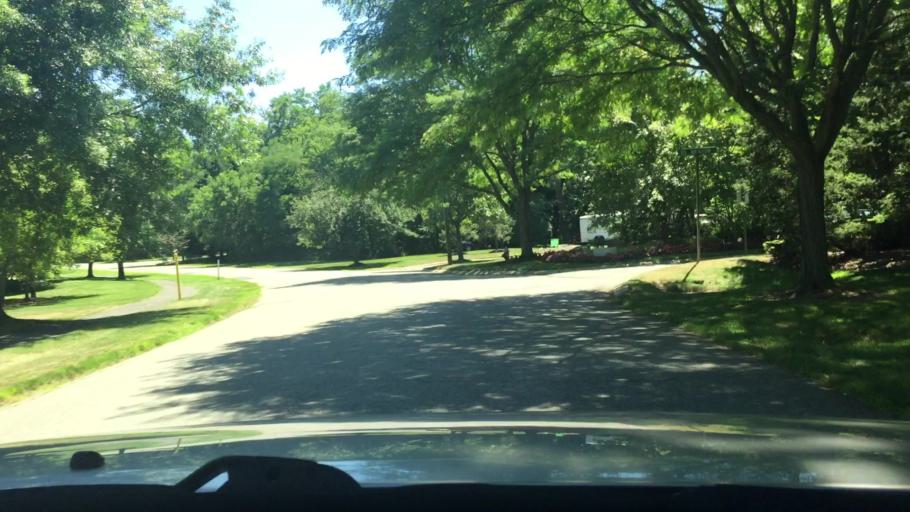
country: US
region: New Jersey
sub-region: Middlesex County
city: East Brunswick
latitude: 40.4224
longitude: -74.3994
